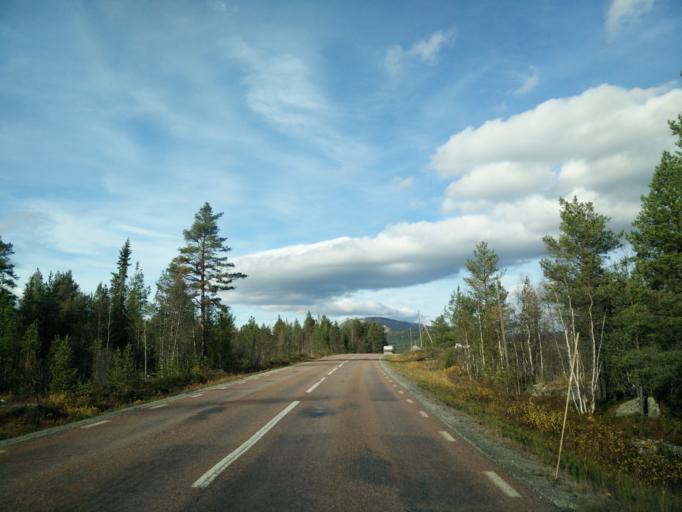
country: NO
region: Hedmark
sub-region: Engerdal
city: Engerdal
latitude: 62.5086
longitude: 12.6111
